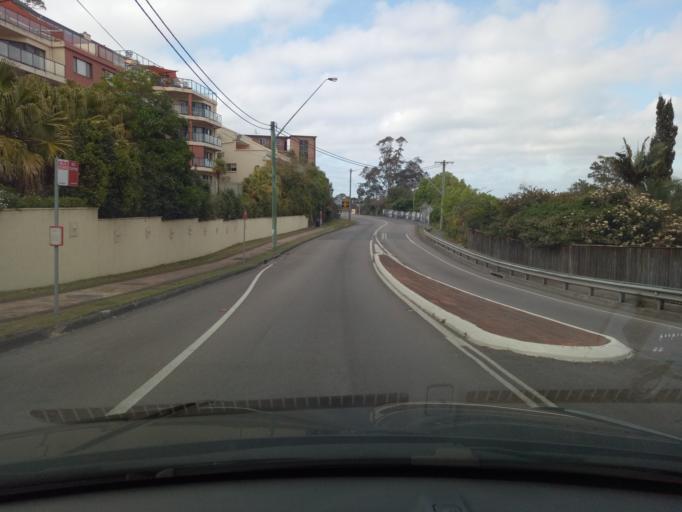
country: AU
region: New South Wales
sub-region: Gosford Shire
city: Gosford
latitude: -33.4294
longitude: 151.3426
